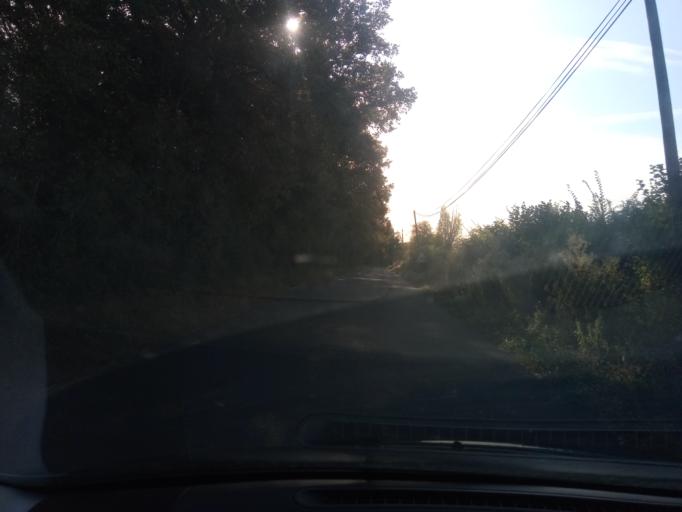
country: FR
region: Poitou-Charentes
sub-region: Departement de la Vienne
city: Montmorillon
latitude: 46.4934
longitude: 0.8168
